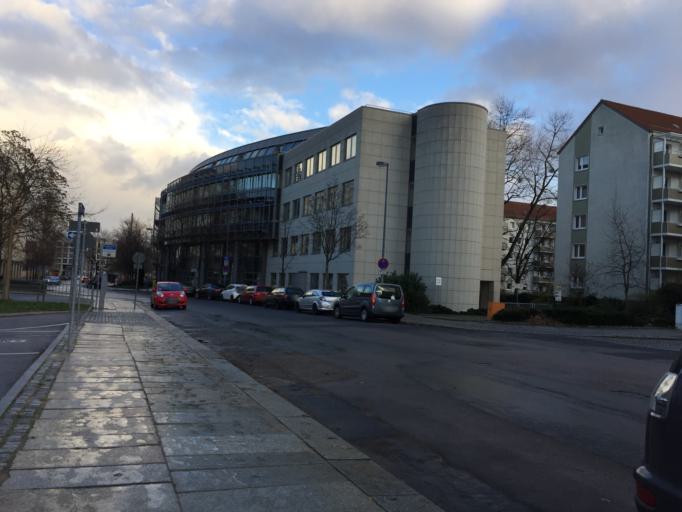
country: DE
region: Saxony
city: Dresden
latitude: 51.0493
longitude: 13.7285
